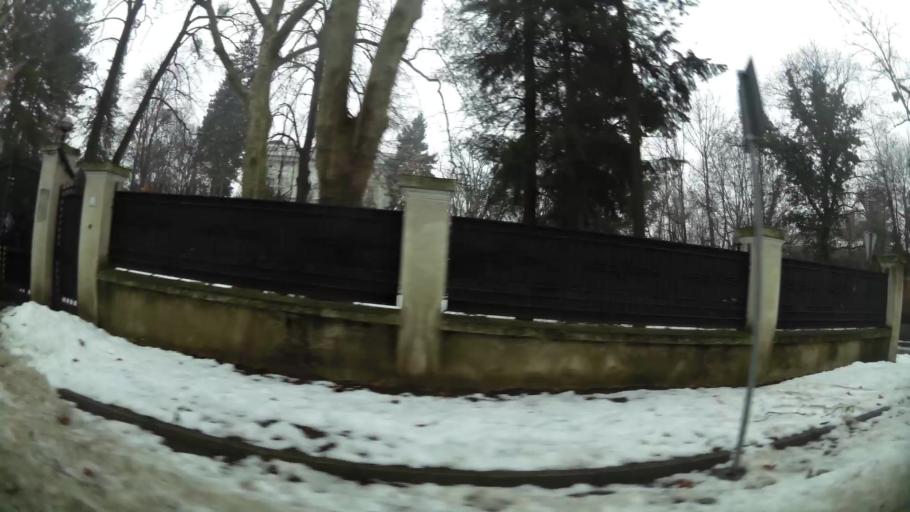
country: RS
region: Central Serbia
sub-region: Belgrade
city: Savski Venac
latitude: 44.7839
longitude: 20.4521
